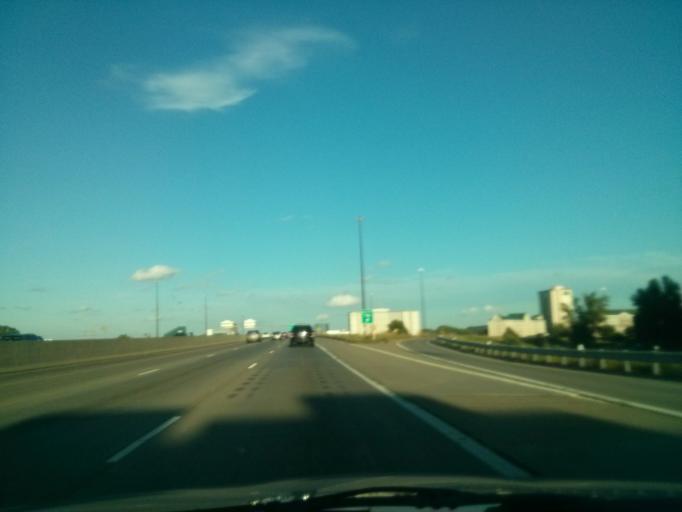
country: US
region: Minnesota
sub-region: Hennepin County
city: Edina
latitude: 44.8590
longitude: -93.3549
